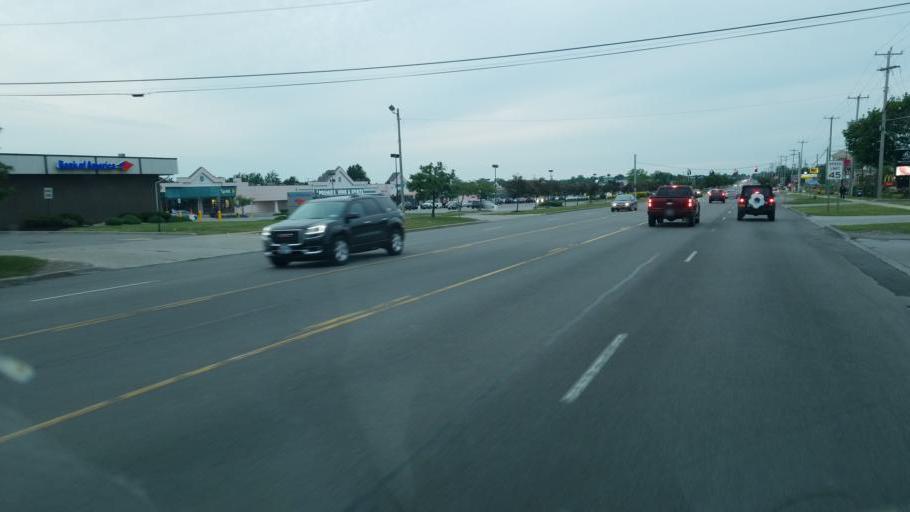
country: US
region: New York
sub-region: Erie County
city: Harris Hill
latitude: 42.9828
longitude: -78.6969
